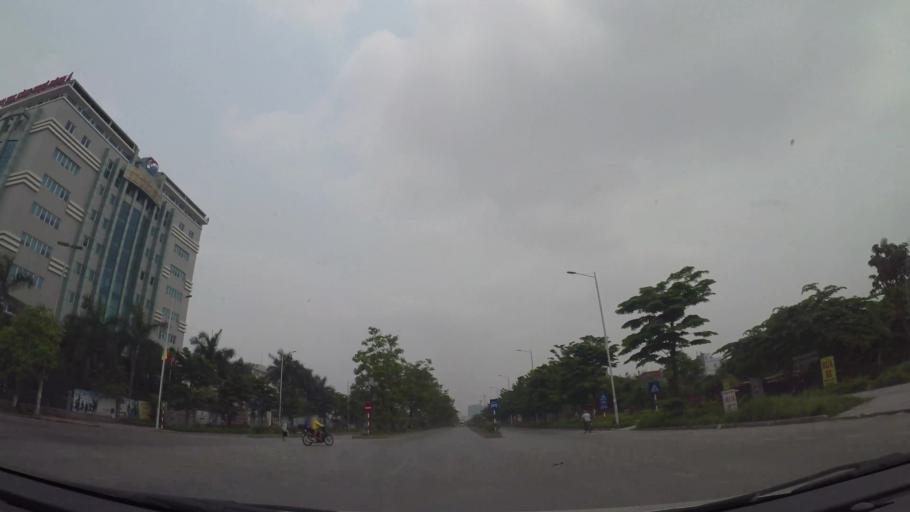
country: VN
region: Ha Noi
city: Cau Dien
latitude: 21.0397
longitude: 105.7415
